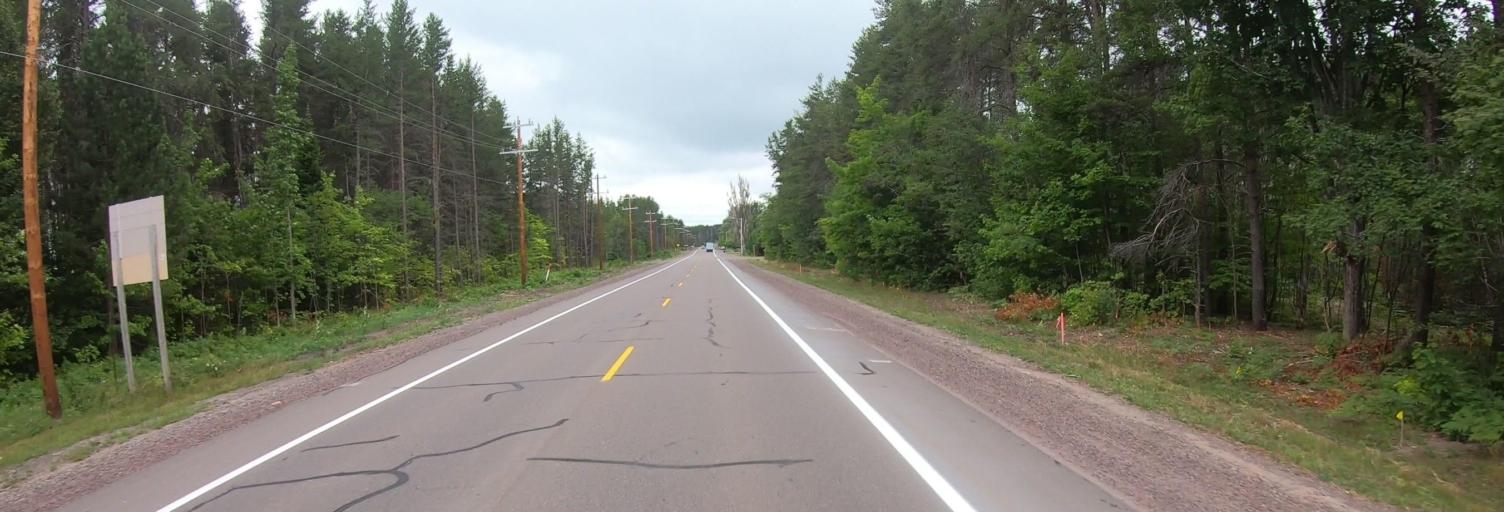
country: US
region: Michigan
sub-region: Houghton County
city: Laurium
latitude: 47.2944
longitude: -88.3967
